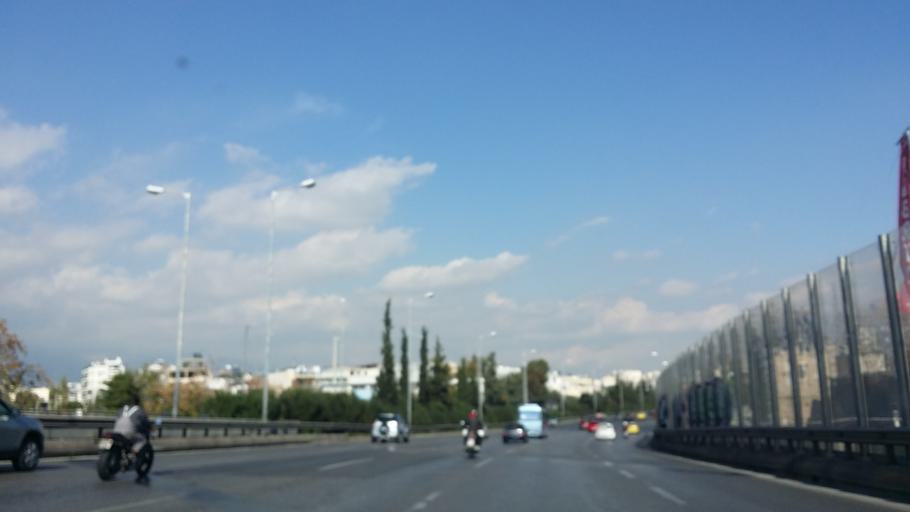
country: GR
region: Attica
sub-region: Nomarchia Athinas
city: Agioi Anargyroi
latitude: 38.0155
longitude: 23.7193
